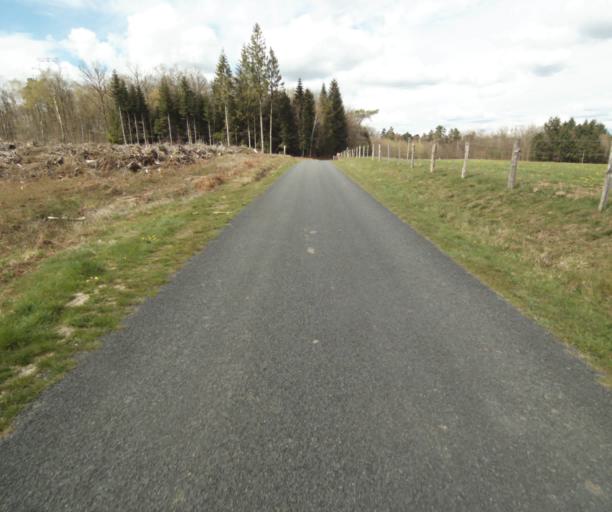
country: FR
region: Limousin
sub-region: Departement de la Correze
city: Argentat
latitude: 45.2052
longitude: 1.9036
